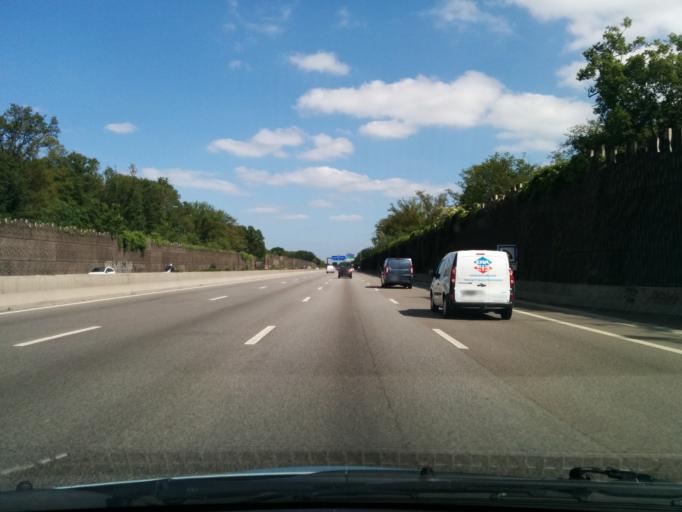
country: FR
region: Ile-de-France
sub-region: Departement des Yvelines
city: Le Chesnay
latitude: 48.8374
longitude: 2.1251
